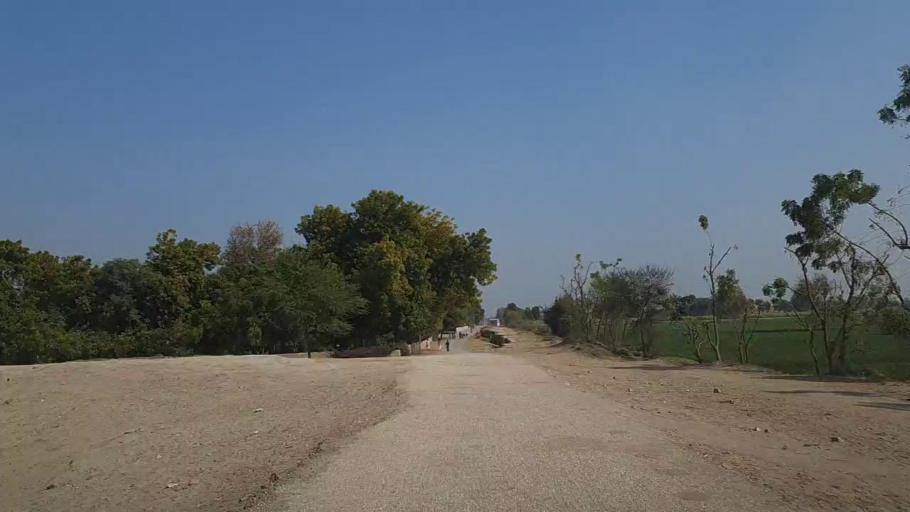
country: PK
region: Sindh
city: Naushahro Firoz
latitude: 26.8599
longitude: 67.9738
